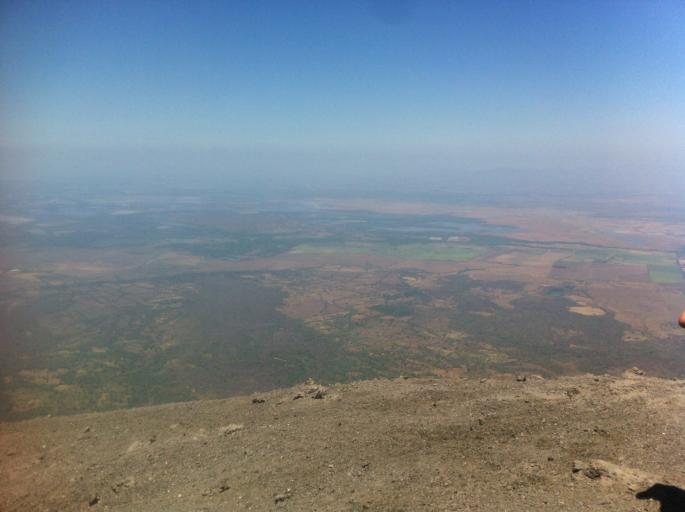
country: NI
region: Chinandega
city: Chichigalpa
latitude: 12.7033
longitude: -87.0061
